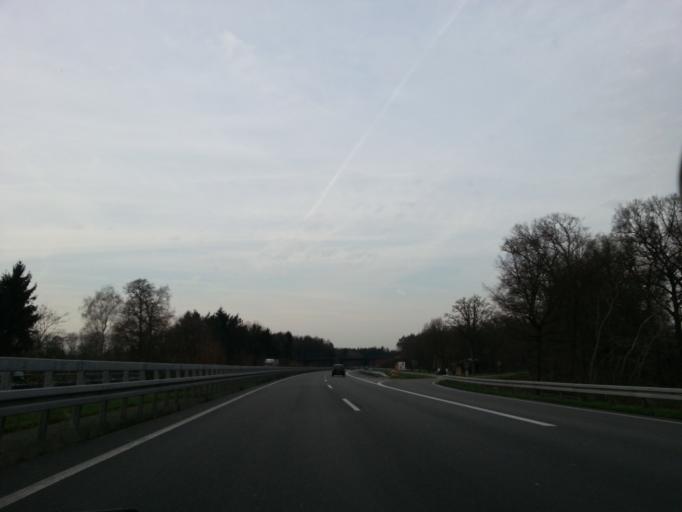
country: DE
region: North Rhine-Westphalia
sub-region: Regierungsbezirk Dusseldorf
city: Mehrhoog
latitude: 51.7807
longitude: 6.5093
